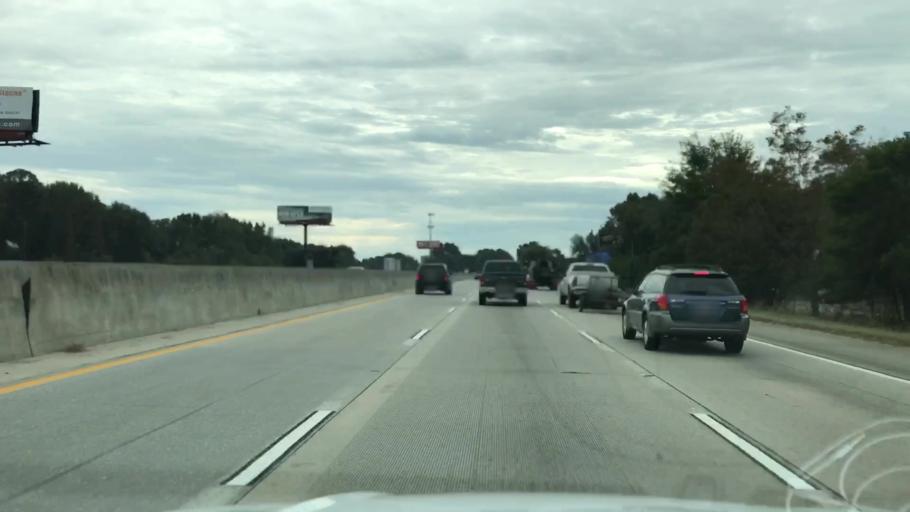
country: US
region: South Carolina
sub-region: Charleston County
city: North Charleston
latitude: 32.8587
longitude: -79.9922
